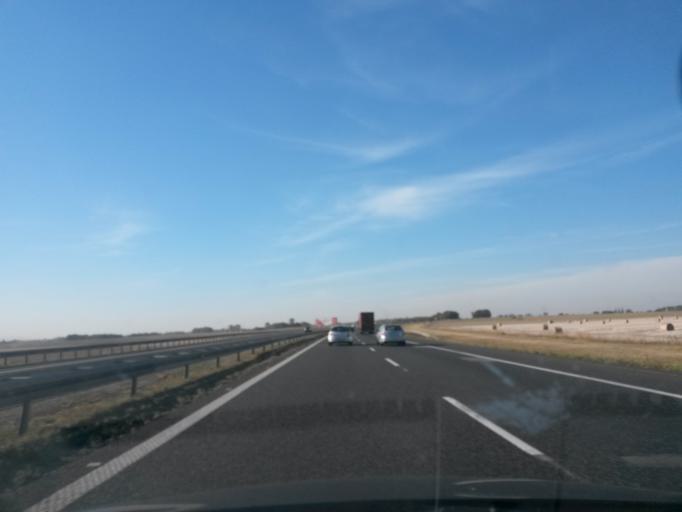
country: PL
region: Opole Voivodeship
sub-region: Powiat brzeski
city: Skarbimierz Osiedle
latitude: 50.7893
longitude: 17.3354
